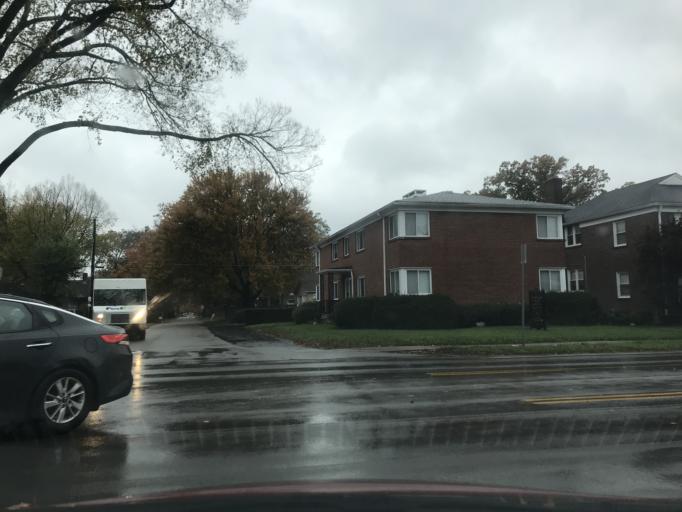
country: US
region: Kentucky
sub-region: Jefferson County
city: Saint Matthews
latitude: 38.2506
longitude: -85.6534
